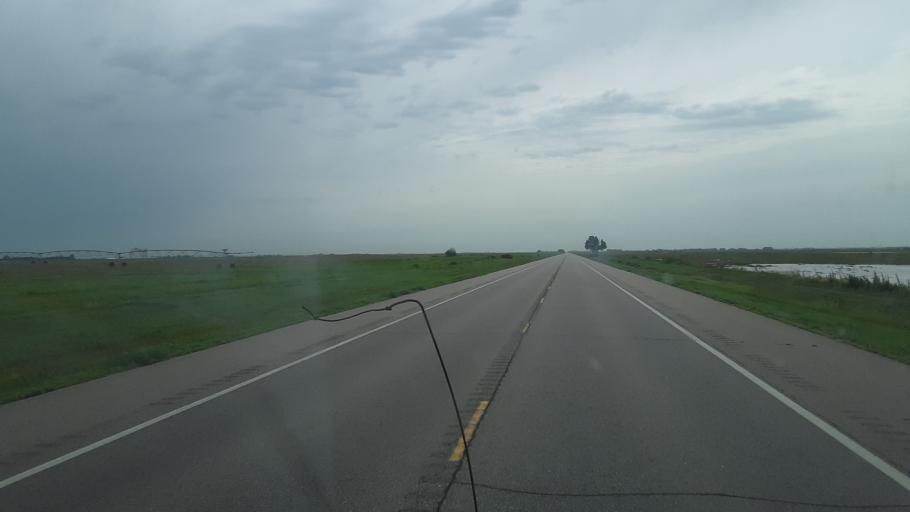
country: US
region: Kansas
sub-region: Stafford County
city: Saint John
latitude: 37.9563
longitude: -98.9126
